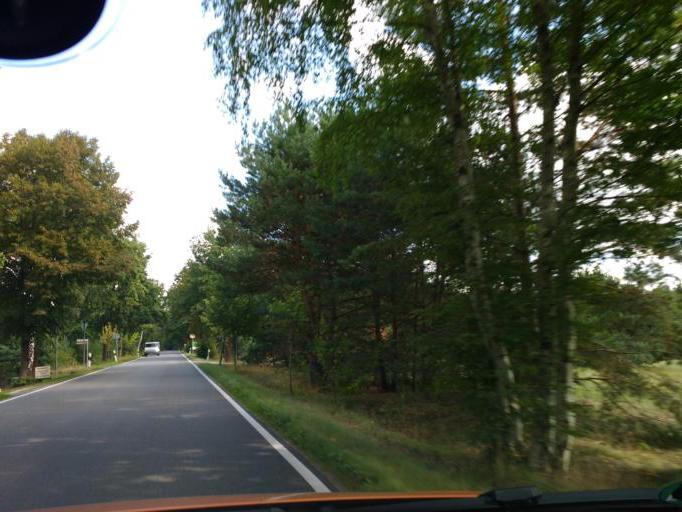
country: DE
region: Brandenburg
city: Wandlitz
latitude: 52.7408
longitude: 13.4024
